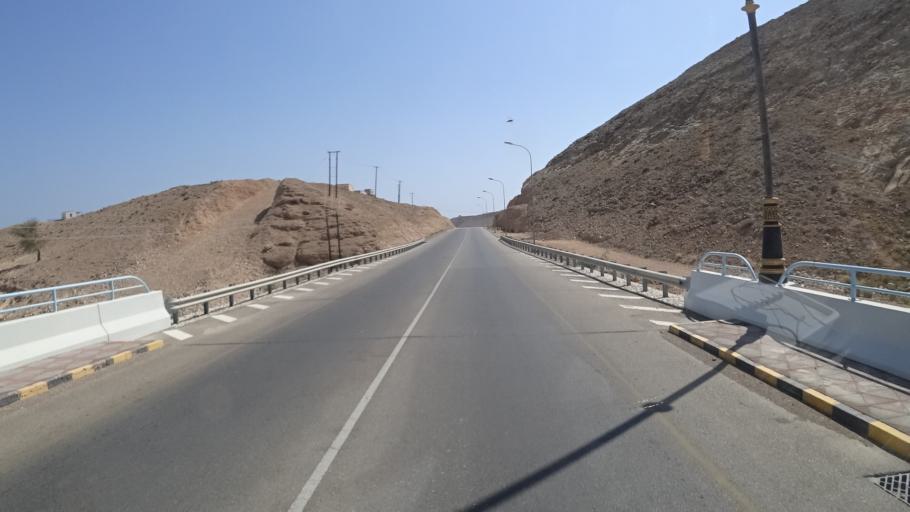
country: OM
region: Ash Sharqiyah
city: Sur
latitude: 22.5508
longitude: 59.5288
